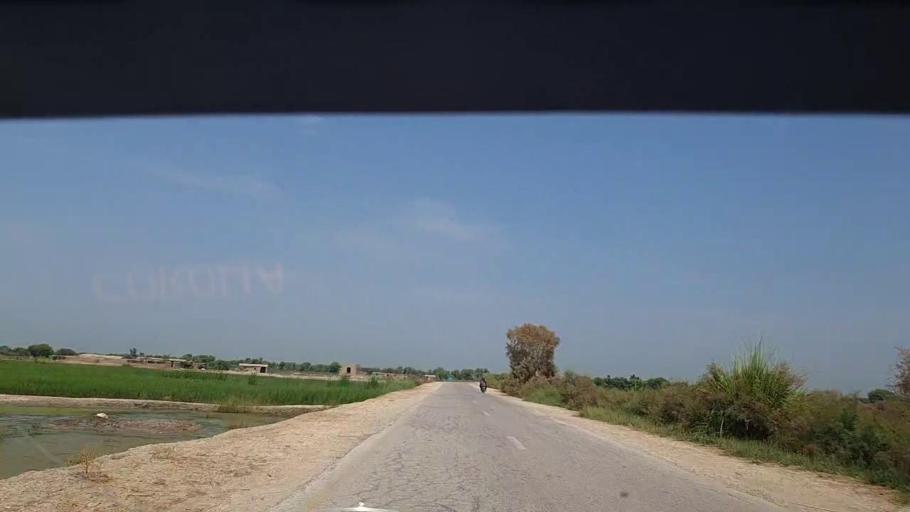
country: PK
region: Sindh
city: Thul
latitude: 28.1369
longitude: 68.8175
